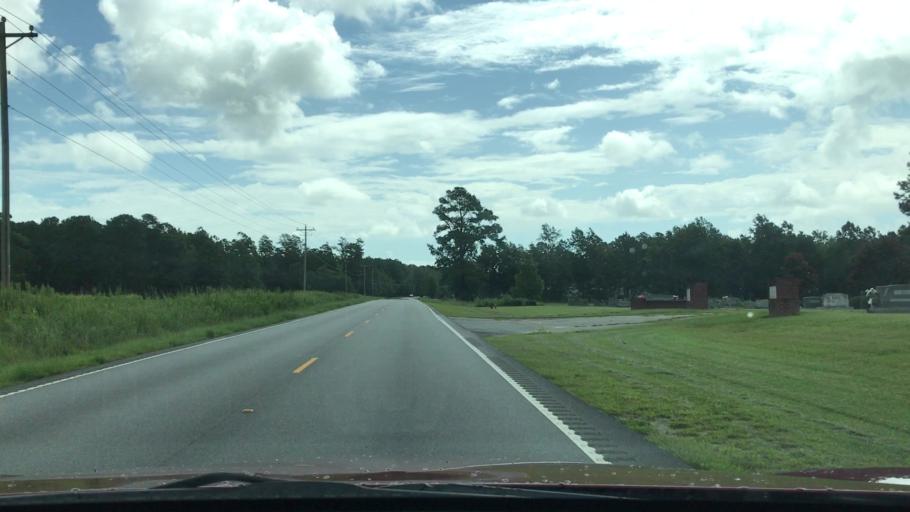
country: US
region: South Carolina
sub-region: Horry County
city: North Myrtle Beach
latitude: 33.9247
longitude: -78.7880
